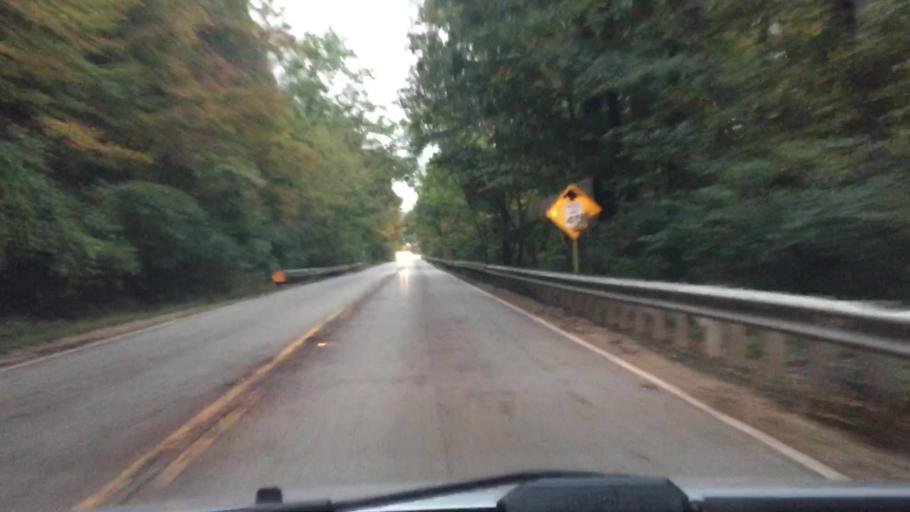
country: US
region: Illinois
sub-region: McHenry County
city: Algonquin
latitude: 42.1489
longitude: -88.2949
